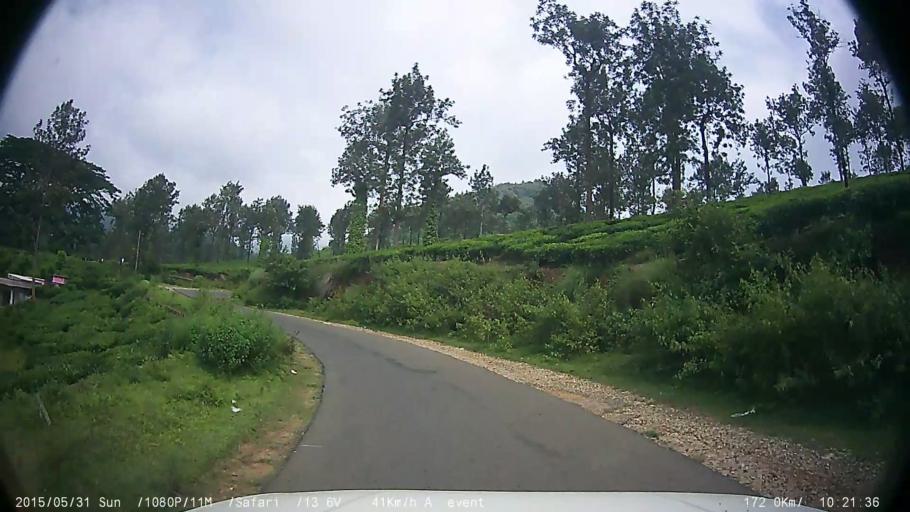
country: IN
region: Kerala
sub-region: Wayanad
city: Kalpetta
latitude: 11.5405
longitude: 76.1372
